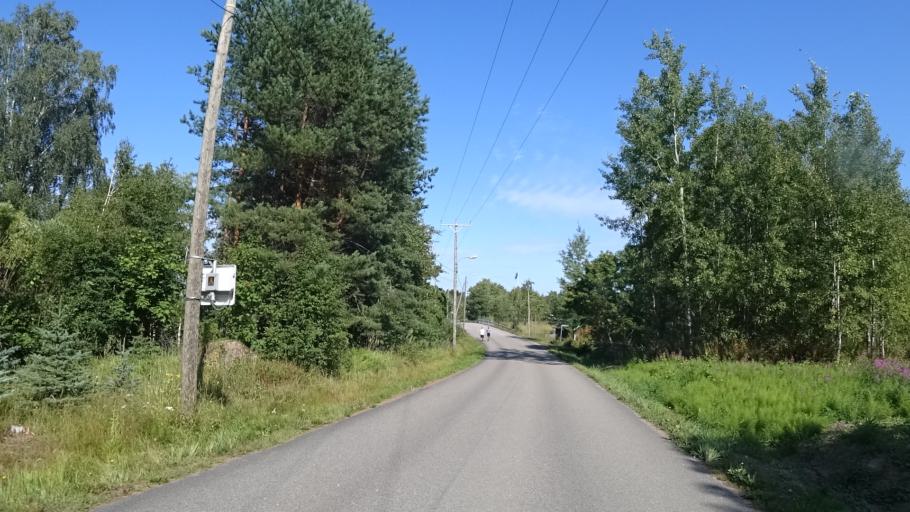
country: FI
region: Kymenlaakso
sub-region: Kotka-Hamina
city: Hamina
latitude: 60.5526
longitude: 27.2001
